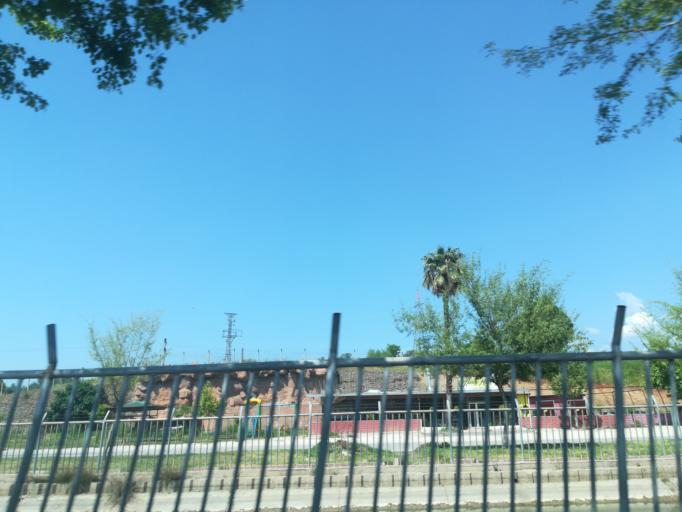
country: TR
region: Adana
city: Adana
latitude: 37.0303
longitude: 35.3516
